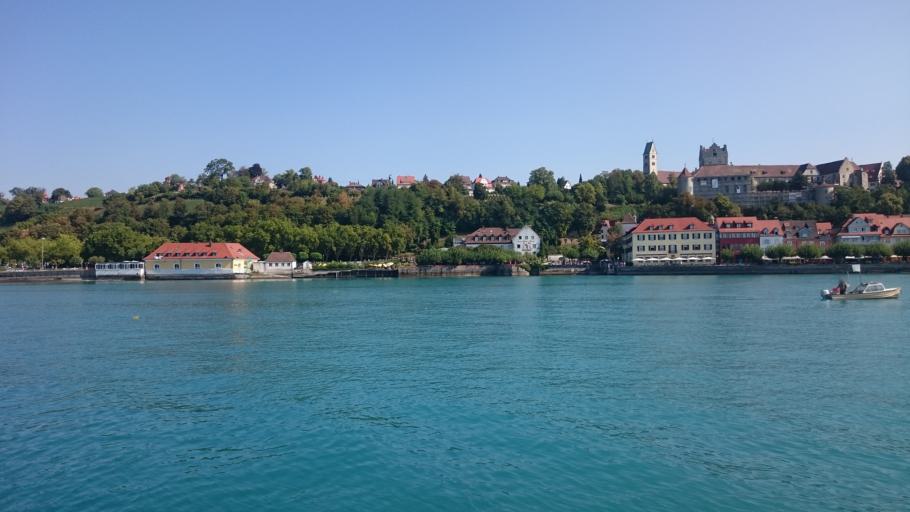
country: DE
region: Baden-Wuerttemberg
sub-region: Tuebingen Region
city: Meersburg
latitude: 47.6914
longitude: 9.2675
